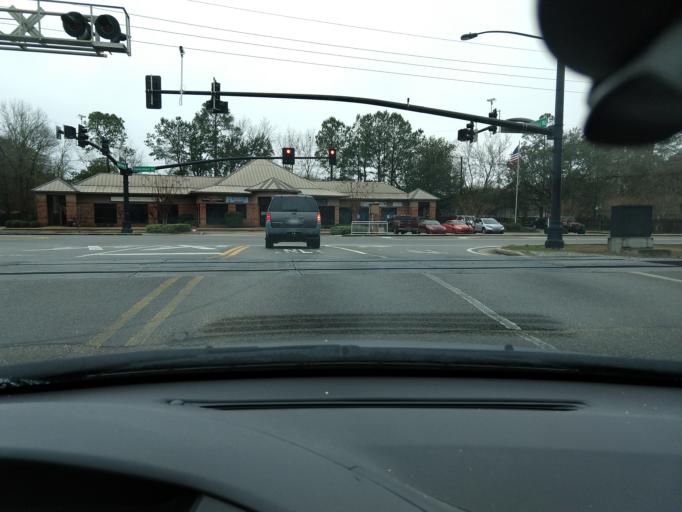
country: US
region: Mississippi
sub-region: Jackson County
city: Gulf Park Estates
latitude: 30.4107
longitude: -88.7859
